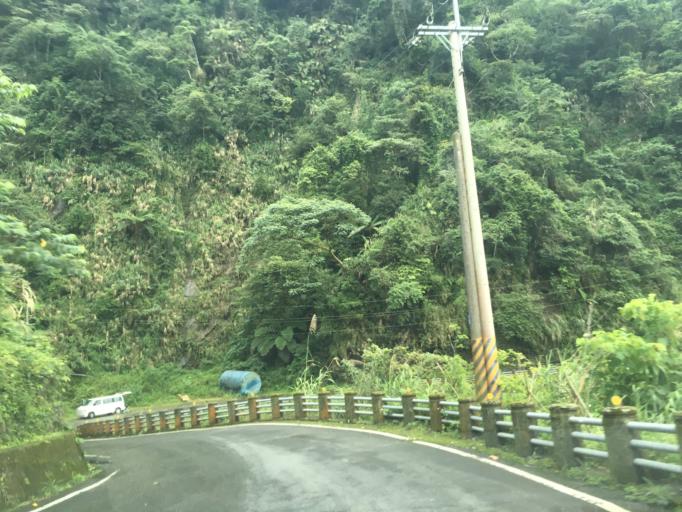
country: TW
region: Taiwan
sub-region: Chiayi
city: Jiayi Shi
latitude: 23.4426
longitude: 120.6587
